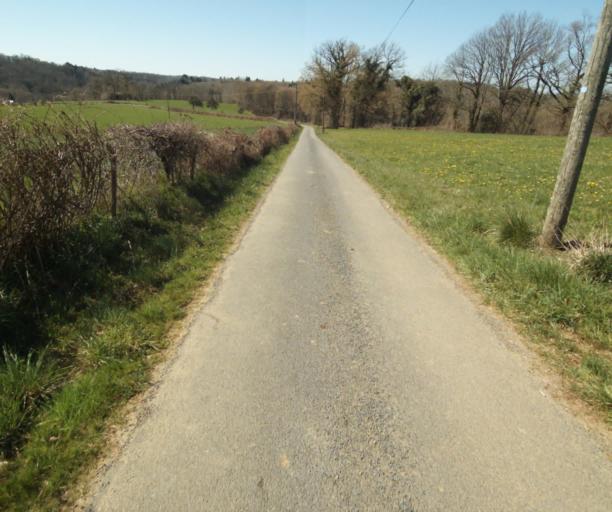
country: FR
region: Limousin
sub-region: Departement de la Correze
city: Chamboulive
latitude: 45.4303
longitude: 1.6828
